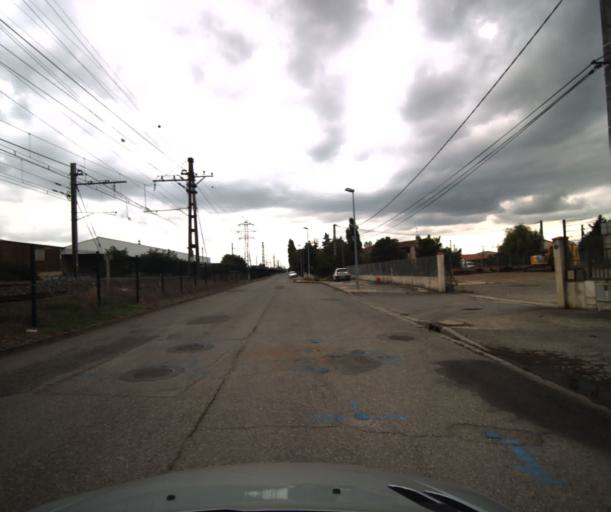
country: FR
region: Midi-Pyrenees
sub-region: Departement de la Haute-Garonne
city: Portet-sur-Garonne
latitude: 43.5414
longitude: 1.4002
